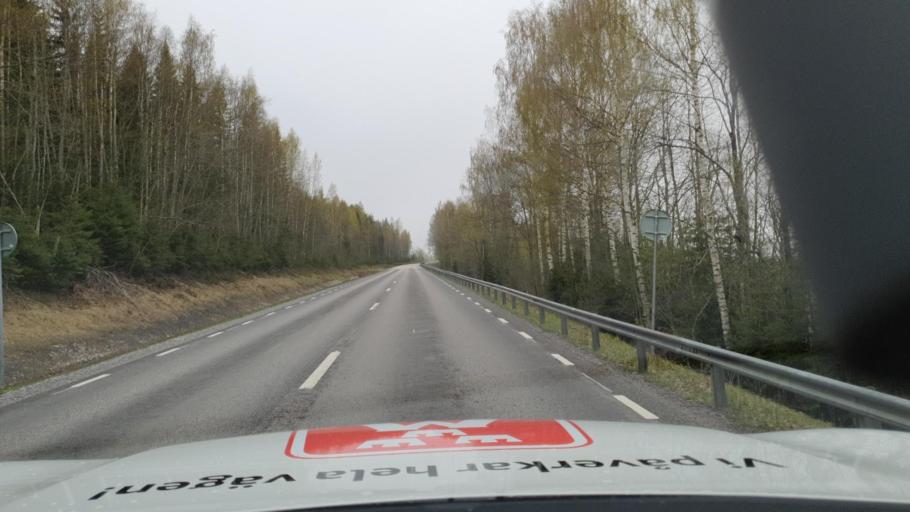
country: SE
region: Vaesterbotten
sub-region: Vannas Kommun
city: Vaennaes
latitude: 63.7868
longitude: 19.8314
